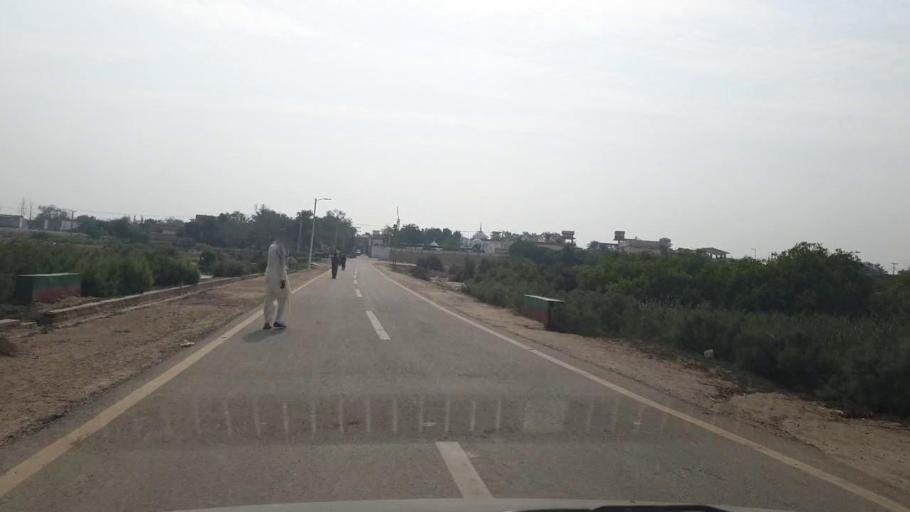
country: PK
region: Sindh
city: Tando Muhammad Khan
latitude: 25.1345
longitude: 68.4534
